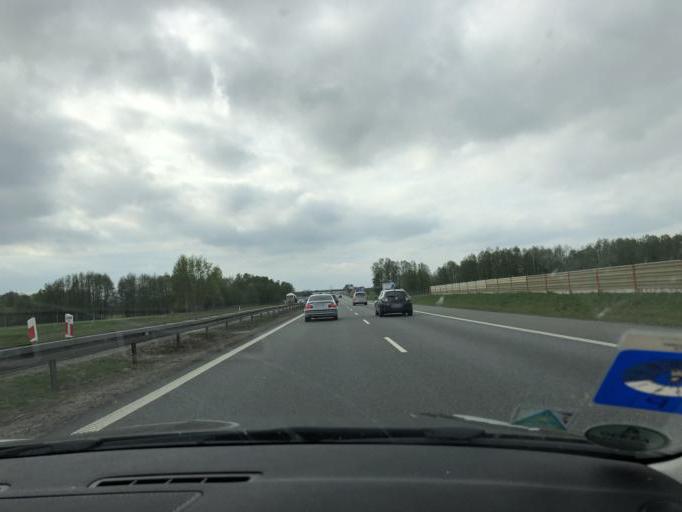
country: PL
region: Opole Voivodeship
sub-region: Powiat opolski
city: Proszkow
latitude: 50.5620
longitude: 17.8731
